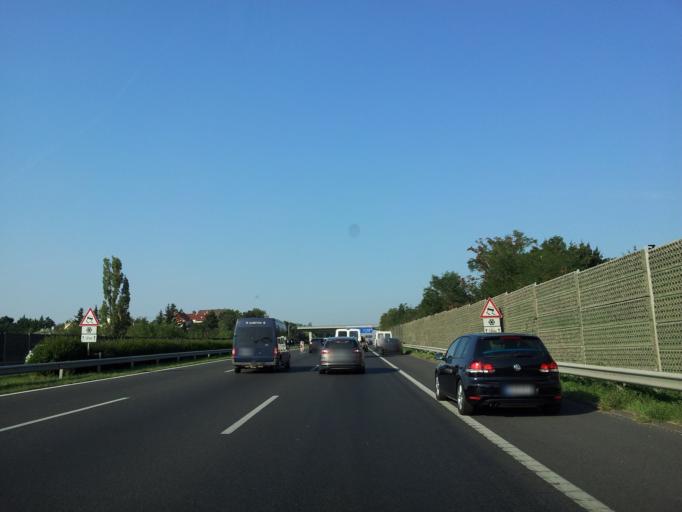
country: HU
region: Pest
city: Toeroekbalint
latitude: 47.4183
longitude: 18.8831
